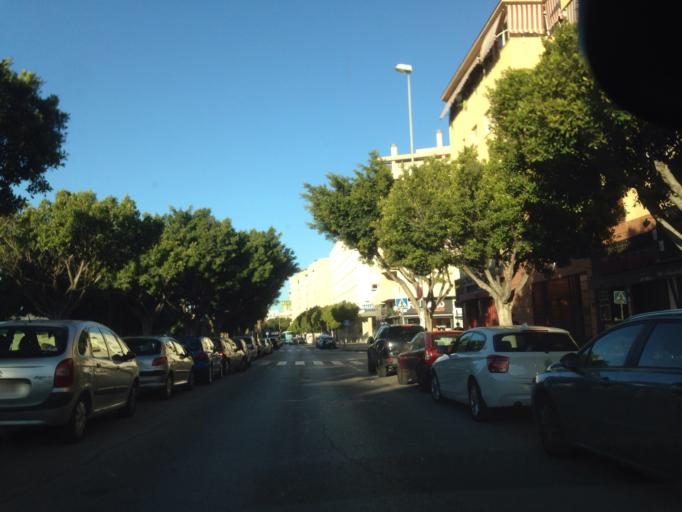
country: ES
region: Andalusia
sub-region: Provincia de Malaga
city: Malaga
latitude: 36.7214
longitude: -4.4772
